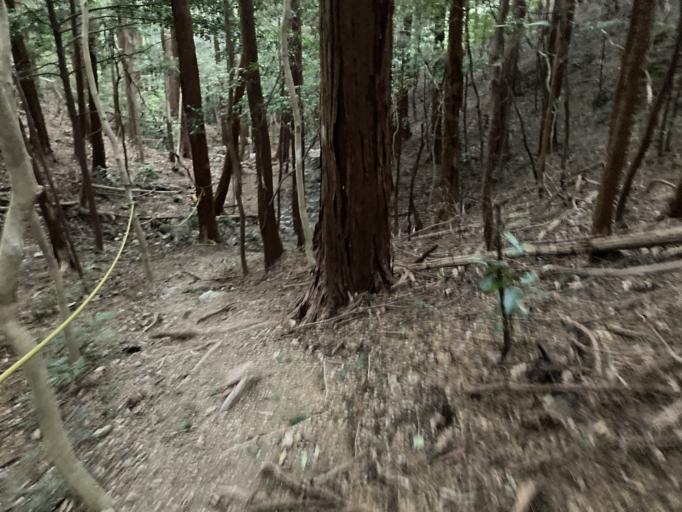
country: JP
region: Aichi
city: Tahara
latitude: 34.6075
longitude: 137.1472
